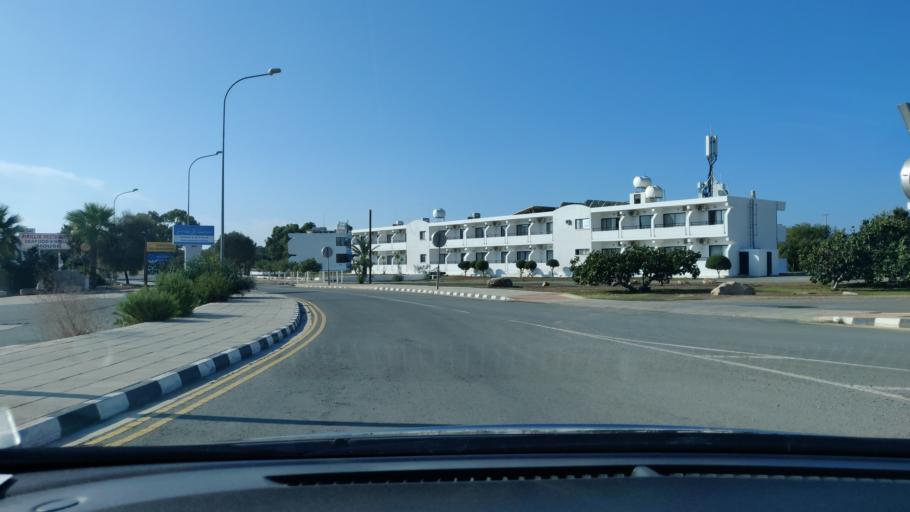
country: CY
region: Ammochostos
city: Protaras
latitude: 34.9853
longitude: 34.0669
